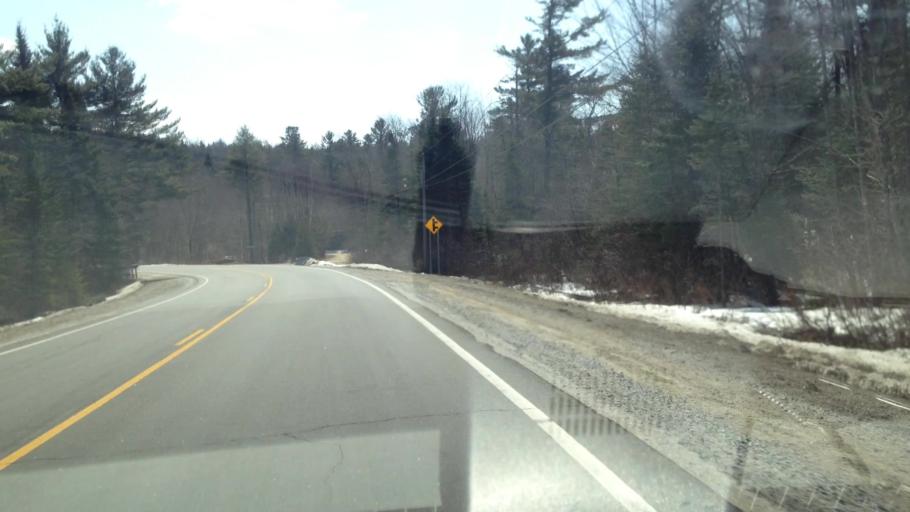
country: US
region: New Hampshire
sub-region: Merrimack County
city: Wilmot
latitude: 43.4656
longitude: -71.9595
